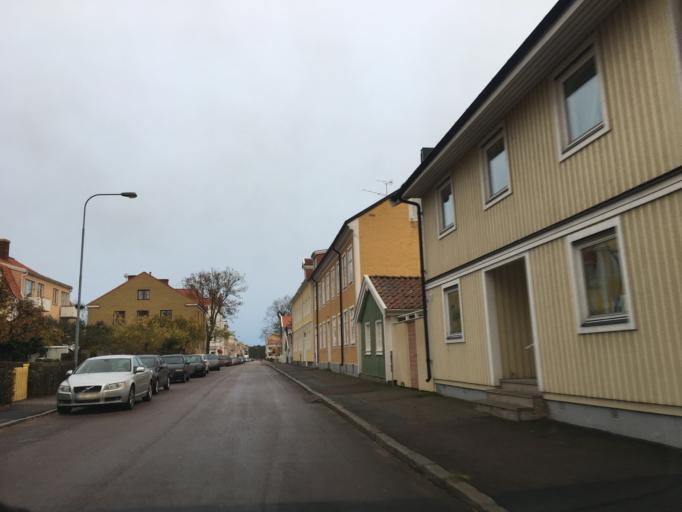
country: SE
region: Kalmar
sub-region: Kalmar Kommun
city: Kalmar
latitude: 56.6691
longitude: 16.3694
